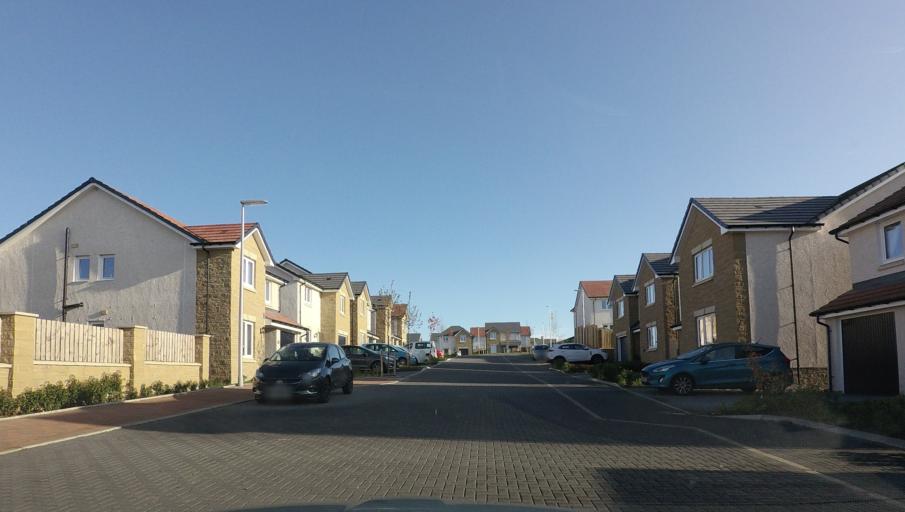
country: GB
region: Scotland
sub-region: Fife
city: Townhill
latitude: 56.0952
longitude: -3.4089
